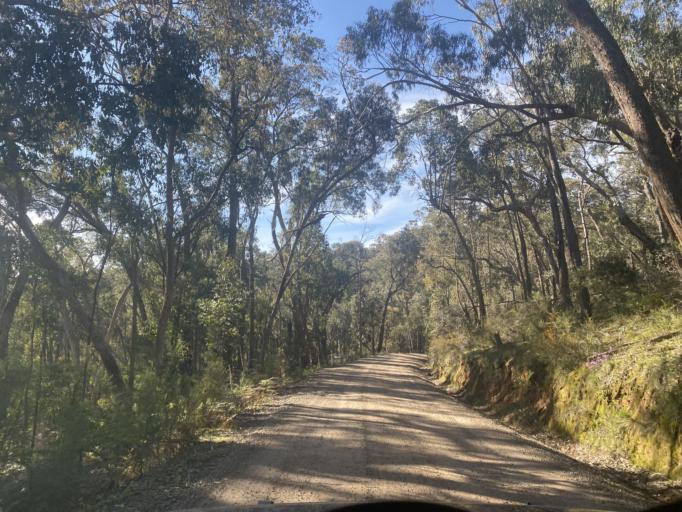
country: AU
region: Victoria
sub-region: Mansfield
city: Mansfield
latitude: -36.8290
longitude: 146.1587
